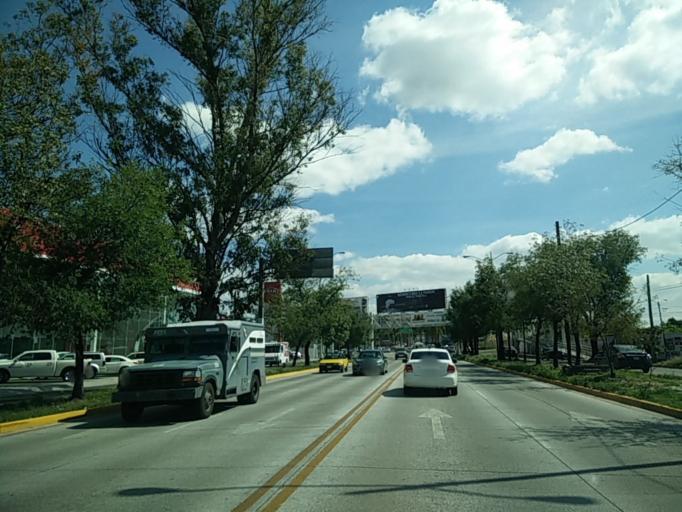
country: MX
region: Jalisco
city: Guadalajara
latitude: 20.6837
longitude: -103.4404
